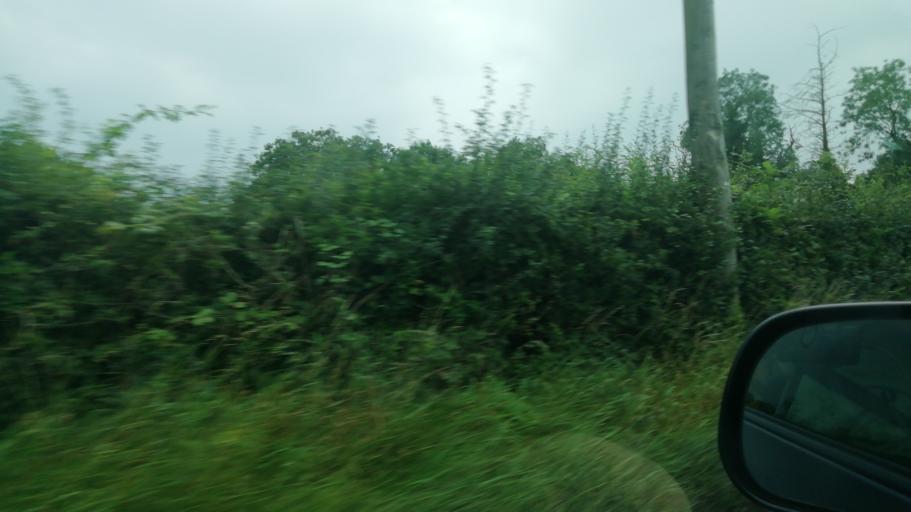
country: IE
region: Munster
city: Fethard
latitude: 52.5162
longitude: -7.6842
